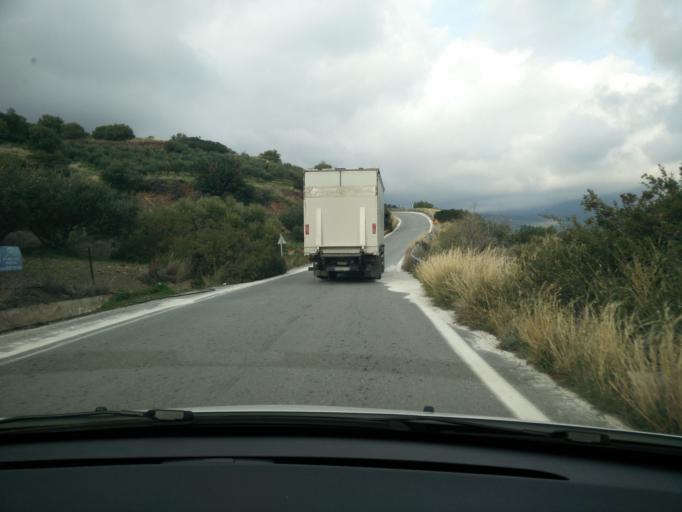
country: GR
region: Crete
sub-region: Nomos Lasithiou
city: Gra Liyia
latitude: 35.0238
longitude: 25.5697
